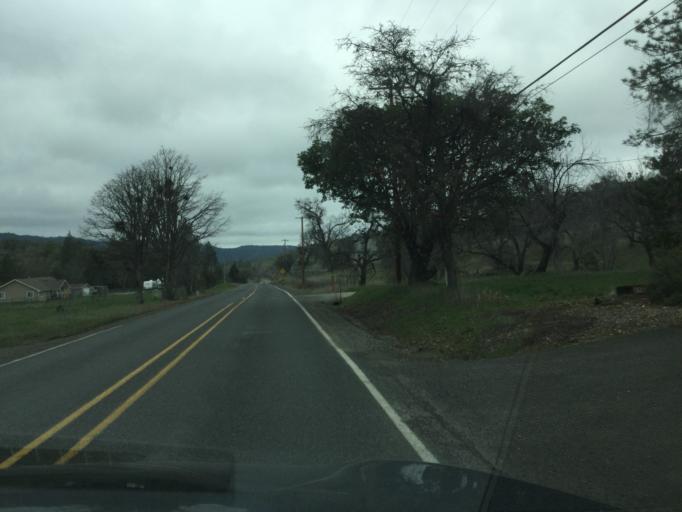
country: US
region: Oregon
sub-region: Jackson County
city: Gold Hill
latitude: 42.3919
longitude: -122.9919
